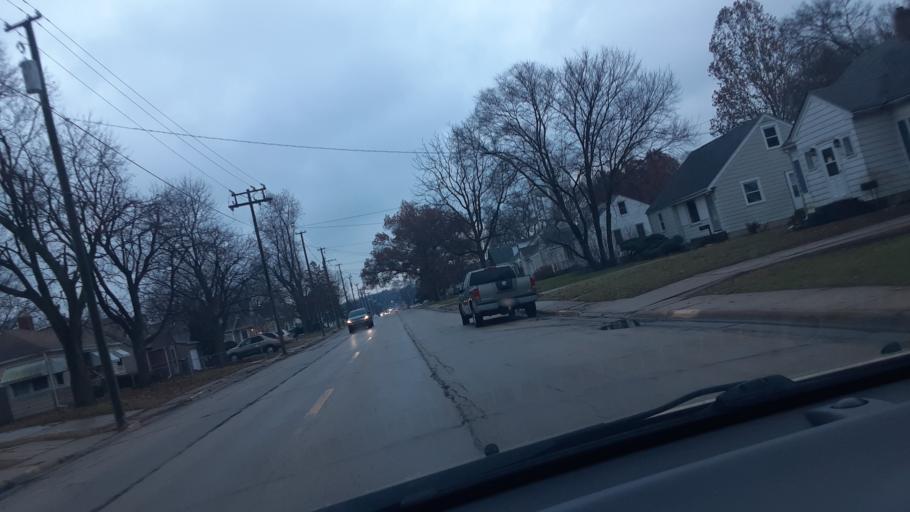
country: US
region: Illinois
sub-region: Winnebago County
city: Loves Park
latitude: 42.3106
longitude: -89.0526
